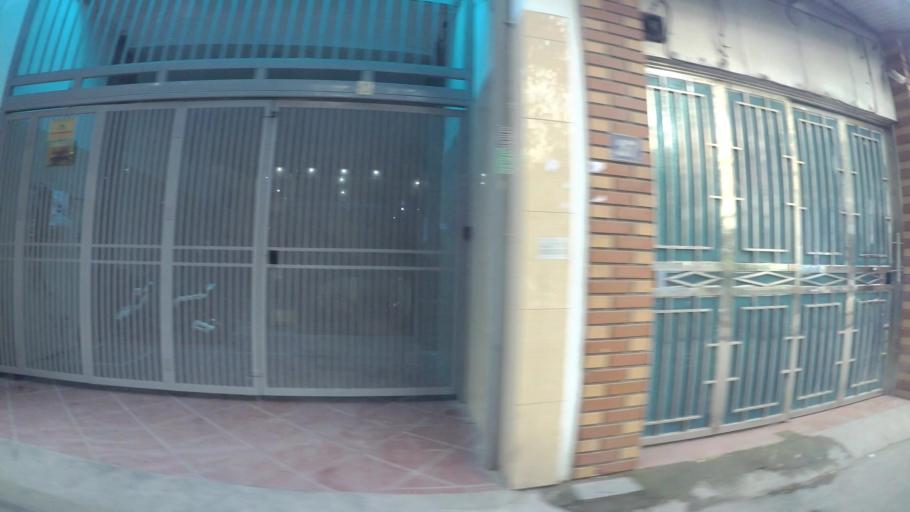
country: VN
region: Ha Noi
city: Tay Ho
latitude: 21.0692
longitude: 105.7917
